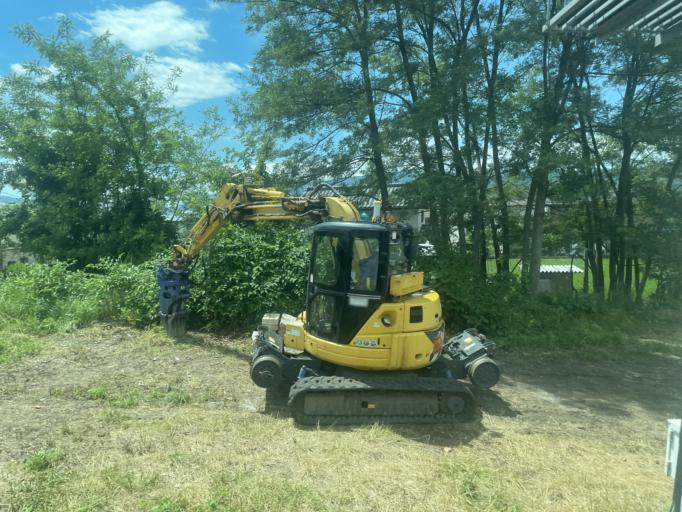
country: JP
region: Nagano
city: Okaya
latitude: 36.0720
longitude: 138.0739
